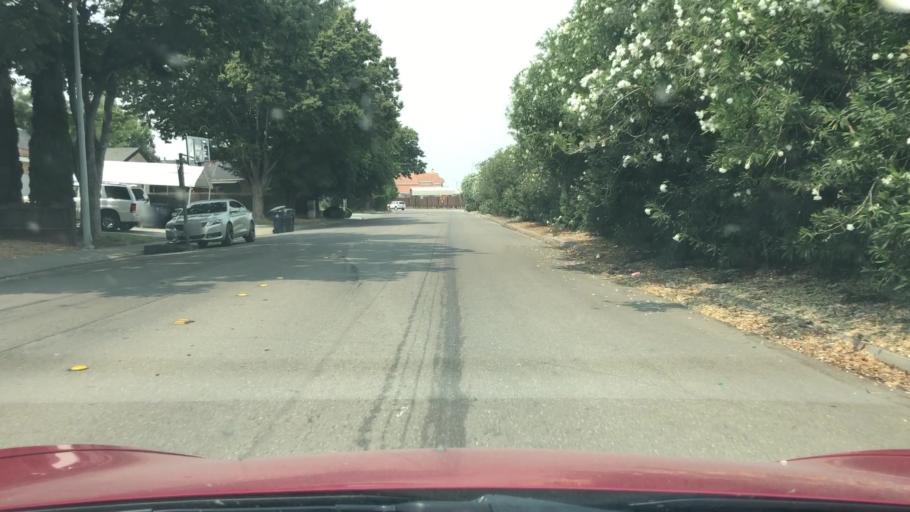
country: US
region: California
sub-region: San Joaquin County
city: Tracy
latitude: 37.7385
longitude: -121.4424
